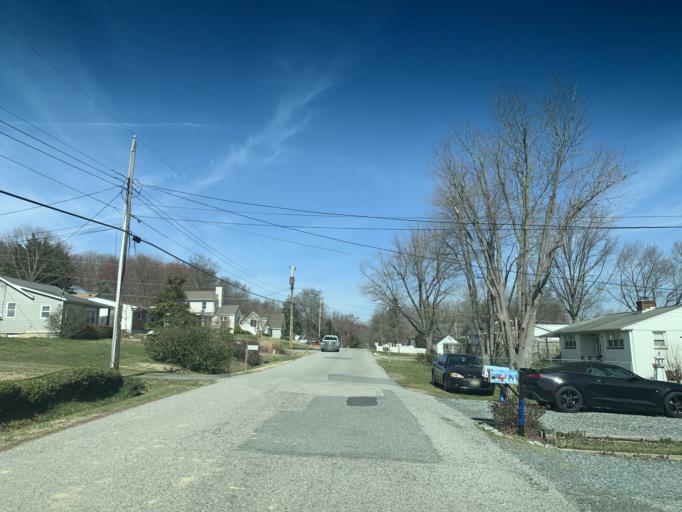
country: US
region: Maryland
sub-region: Cecil County
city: Charlestown
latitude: 39.5431
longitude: -76.0062
